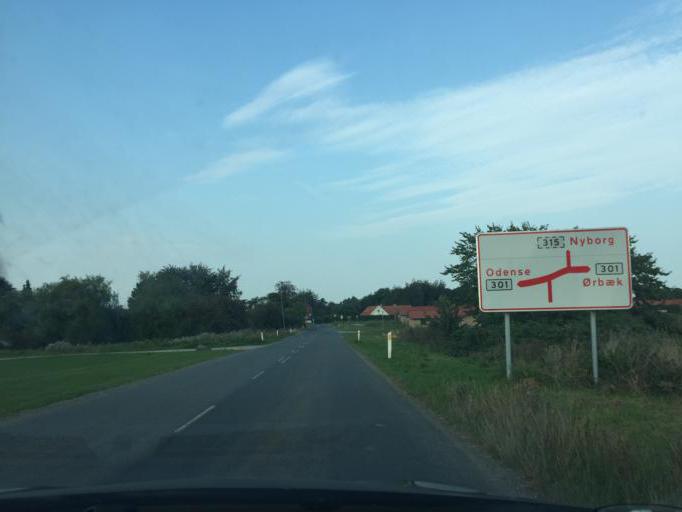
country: DK
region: South Denmark
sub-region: Kerteminde Kommune
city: Langeskov
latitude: 55.3063
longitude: 10.5839
